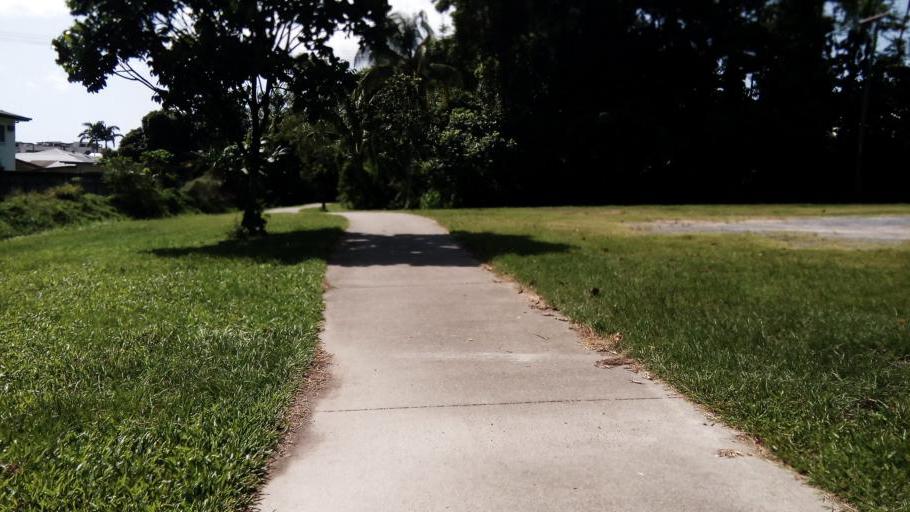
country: AU
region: Queensland
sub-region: Cairns
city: Cairns
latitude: -16.9172
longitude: 145.7637
